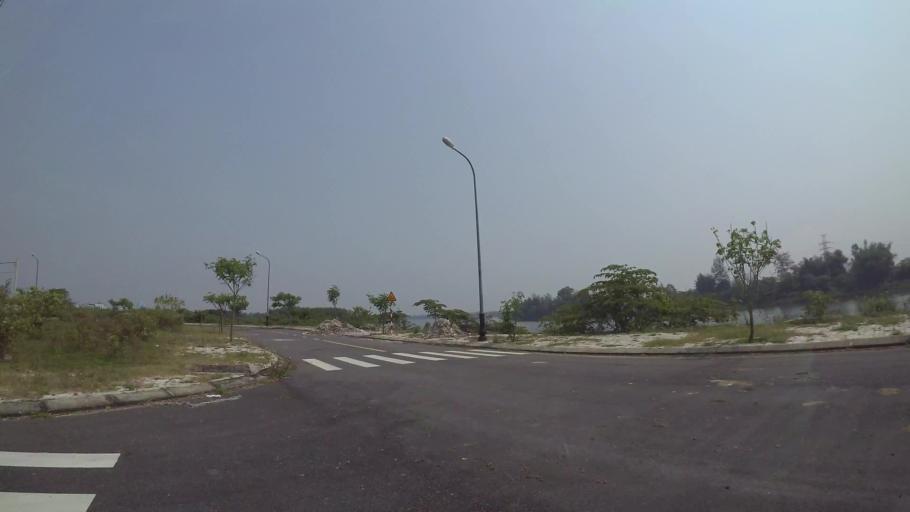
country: VN
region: Da Nang
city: Cam Le
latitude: 15.9705
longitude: 108.2157
